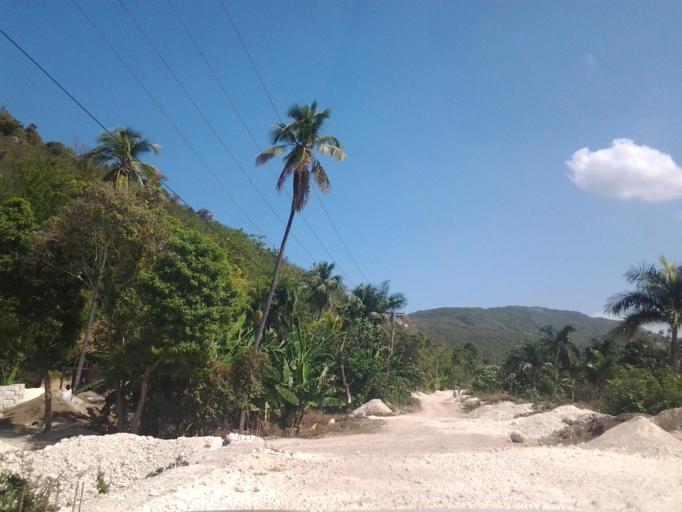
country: HT
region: Ouest
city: Tigwav
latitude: 18.4403
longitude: -72.8430
